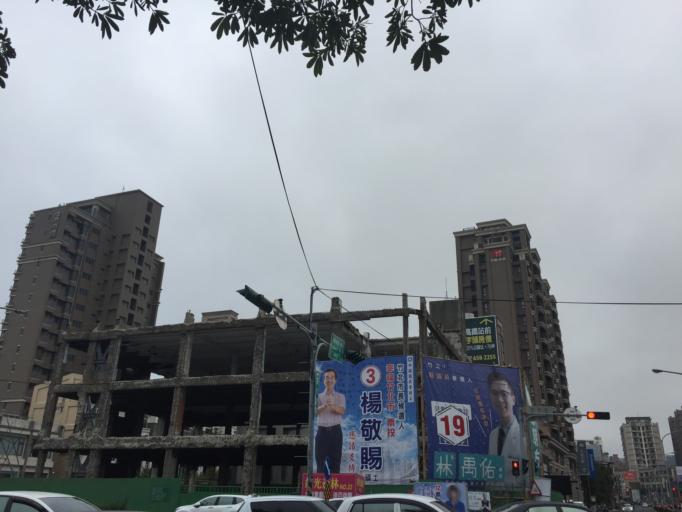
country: TW
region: Taiwan
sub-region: Hsinchu
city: Zhubei
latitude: 24.8193
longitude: 121.0213
